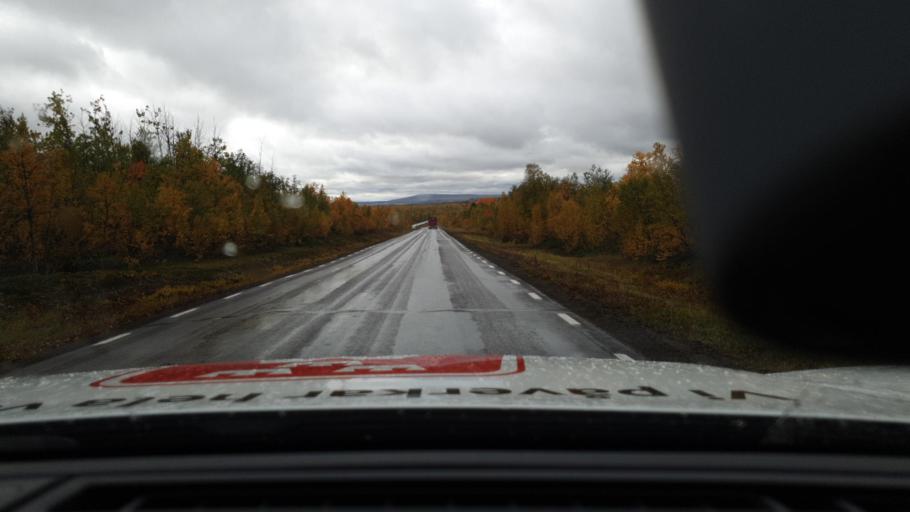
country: SE
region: Norrbotten
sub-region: Kiruna Kommun
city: Kiruna
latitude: 67.7922
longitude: 20.2310
